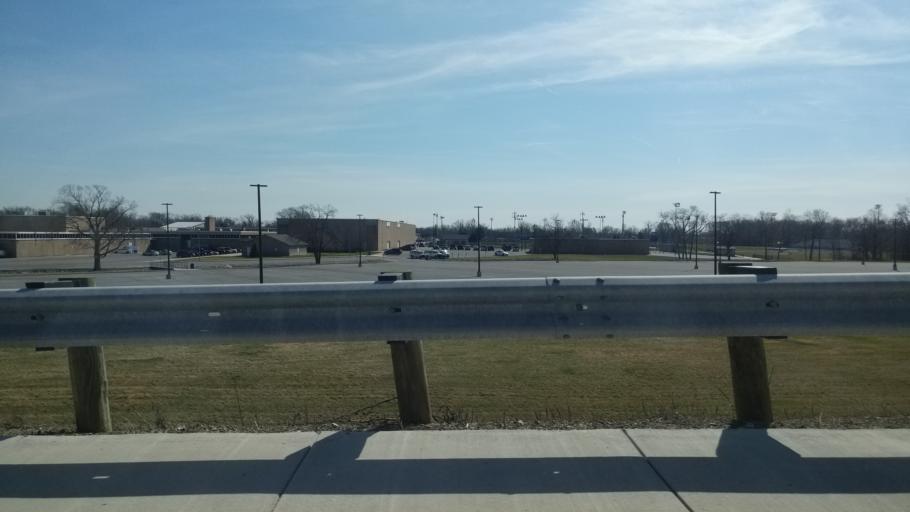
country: US
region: Ohio
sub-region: Hancock County
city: Findlay
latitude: 41.0586
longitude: -83.6671
